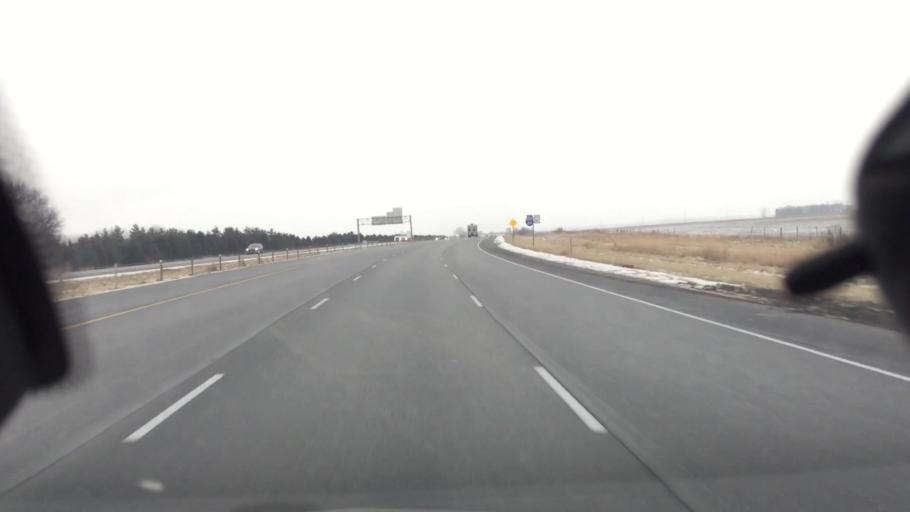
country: US
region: Iowa
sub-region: Scott County
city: Eldridge
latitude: 41.6033
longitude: -90.6665
